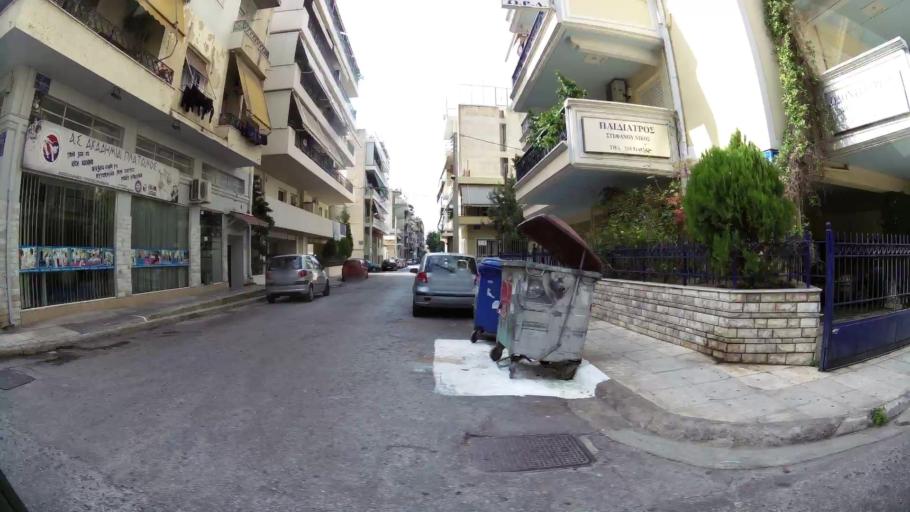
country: GR
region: Attica
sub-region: Nomarchia Athinas
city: Athens
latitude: 37.9912
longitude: 23.7107
